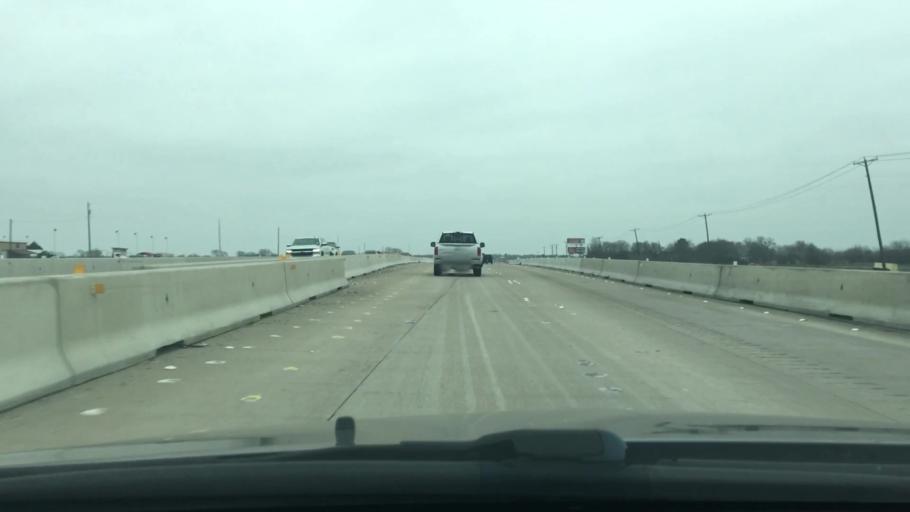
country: US
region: Texas
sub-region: Navarro County
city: Corsicana
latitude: 32.0353
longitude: -96.4448
